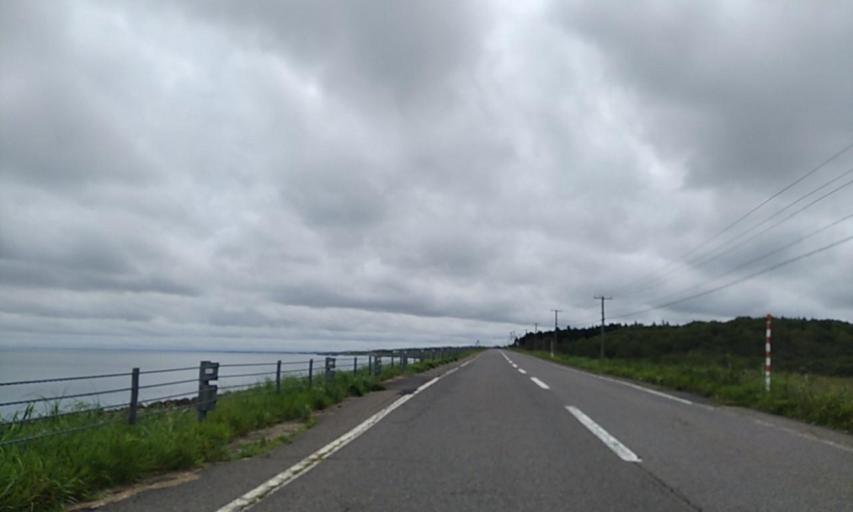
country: JP
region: Hokkaido
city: Shibetsu
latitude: 43.4428
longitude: 145.2621
